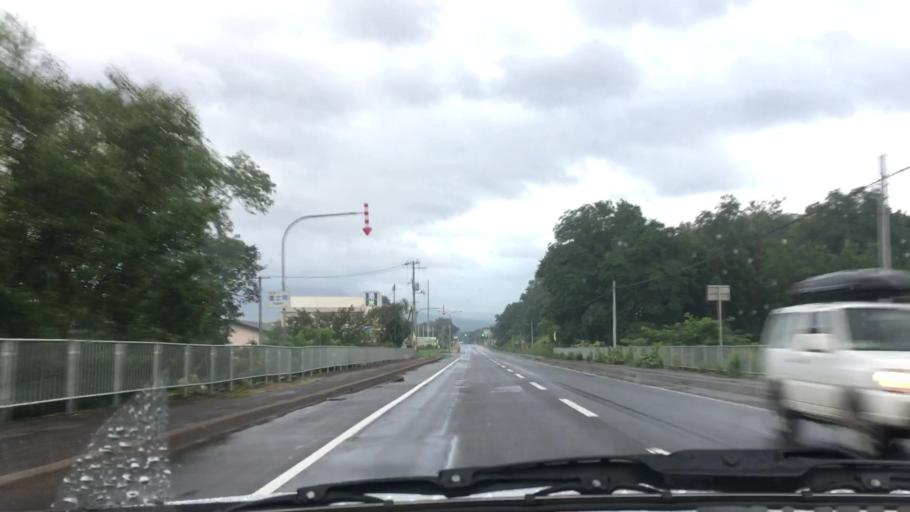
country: JP
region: Hokkaido
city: Nanae
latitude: 42.1137
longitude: 140.5447
